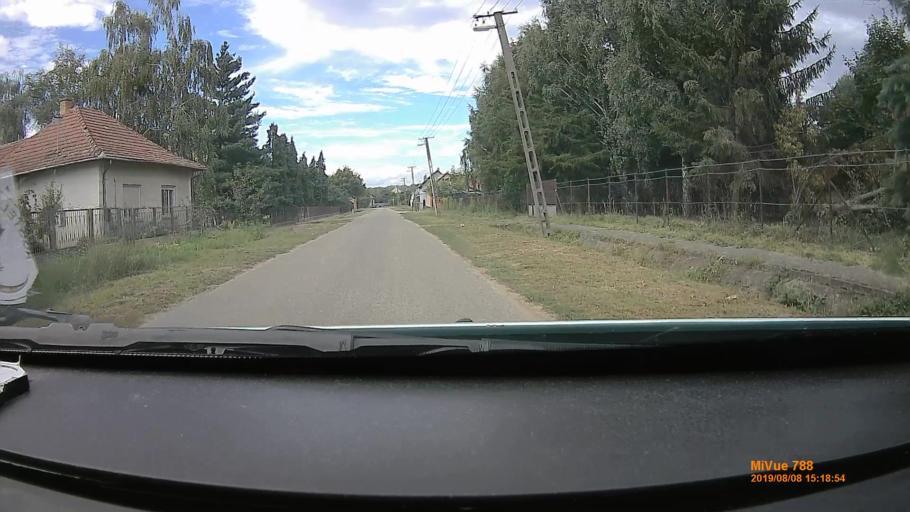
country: HU
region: Szabolcs-Szatmar-Bereg
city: Tunyogmatolcs
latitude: 47.9688
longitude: 22.4581
